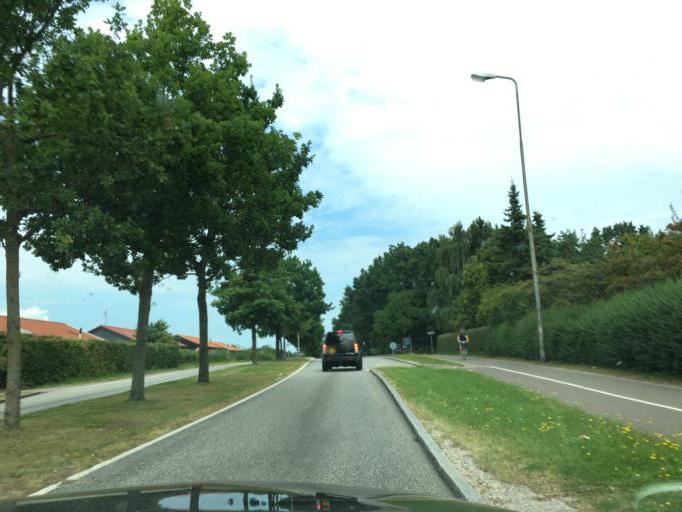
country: DK
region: Capital Region
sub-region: Fredensborg Kommune
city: Kokkedal
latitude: 55.8971
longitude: 12.4990
